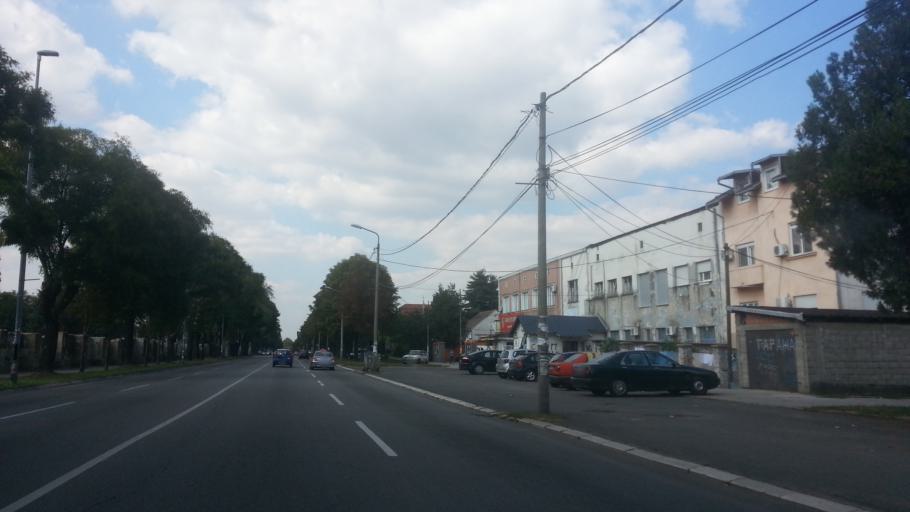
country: RS
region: Central Serbia
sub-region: Belgrade
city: Zemun
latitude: 44.8557
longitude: 20.3854
